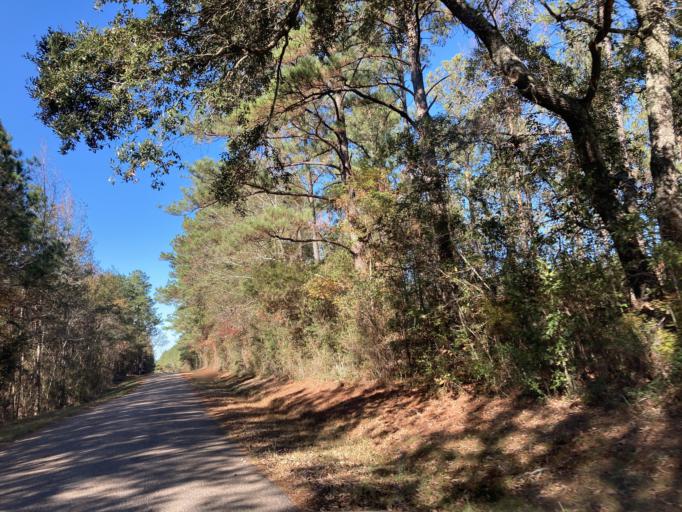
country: US
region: Mississippi
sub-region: Lamar County
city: Sumrall
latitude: 31.3091
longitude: -89.6069
